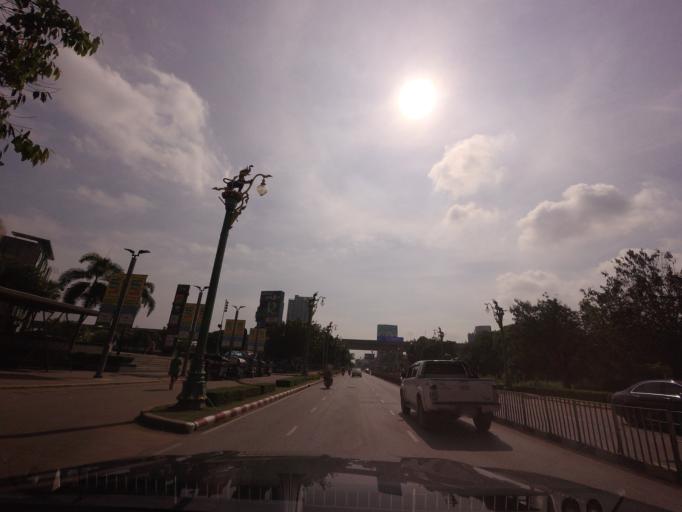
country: TH
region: Khon Kaen
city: Khon Kaen
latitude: 16.4318
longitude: 102.8256
